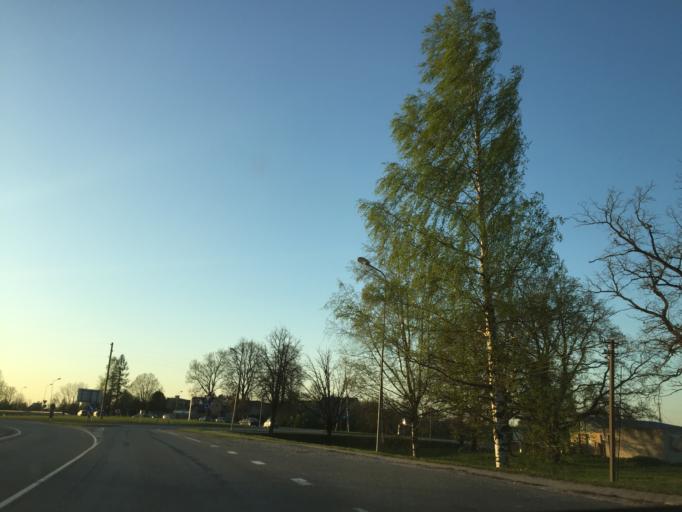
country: LV
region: Ikskile
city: Ikskile
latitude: 56.8638
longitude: 24.5614
